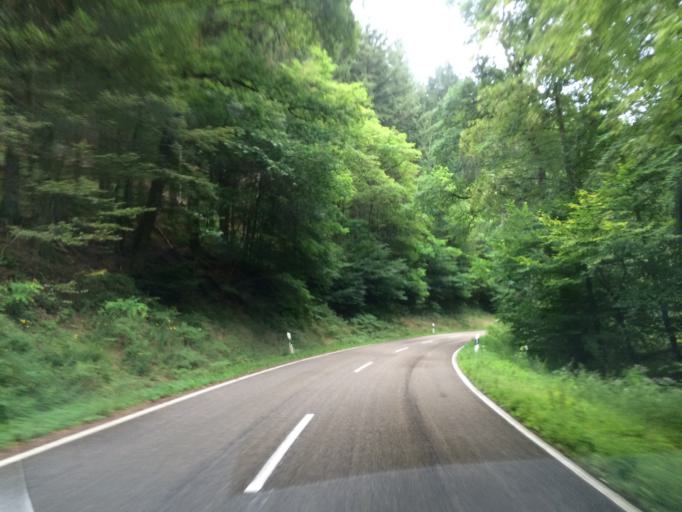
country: DE
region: Rheinland-Pfalz
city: Bobenthal
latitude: 49.0479
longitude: 7.8792
